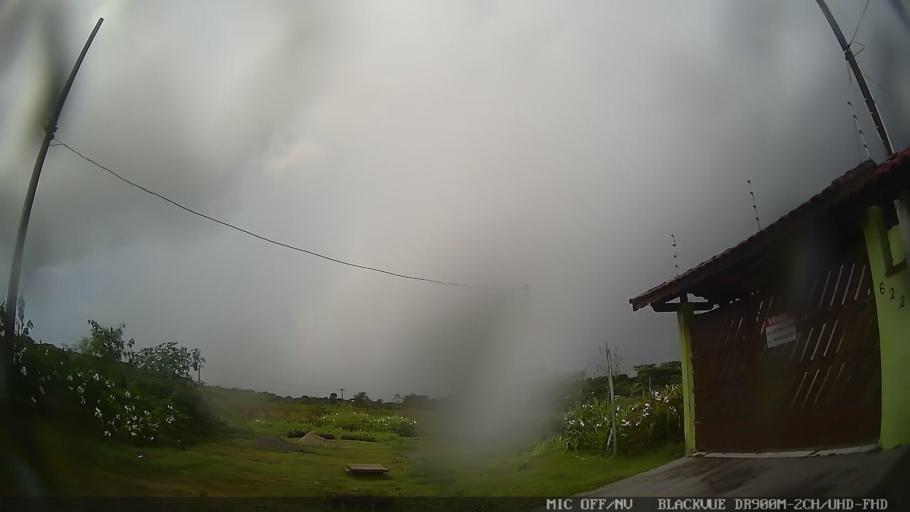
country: BR
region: Sao Paulo
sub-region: Peruibe
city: Peruibe
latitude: -24.2388
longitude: -46.9023
